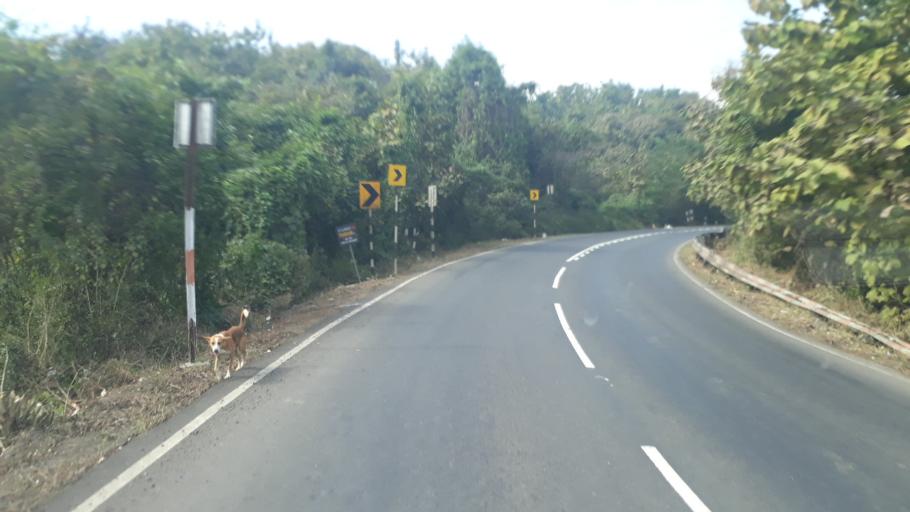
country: IN
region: Maharashtra
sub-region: Raigarh
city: Alibag
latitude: 18.6950
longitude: 72.9360
